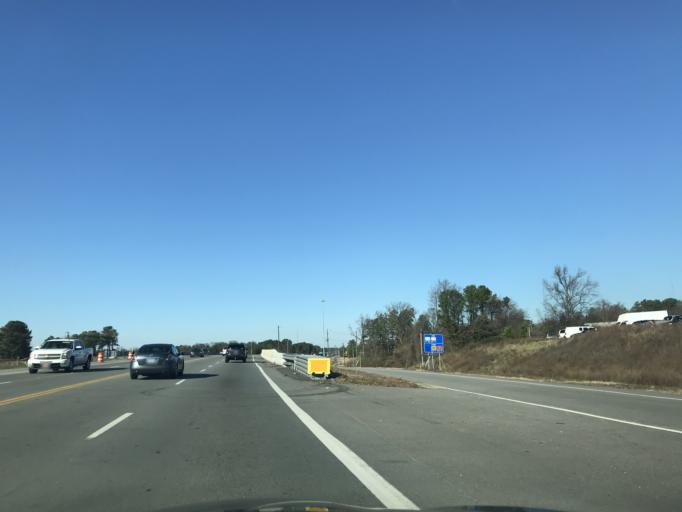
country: US
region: North Carolina
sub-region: Durham County
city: Durham
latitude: 35.9885
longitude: -78.8617
